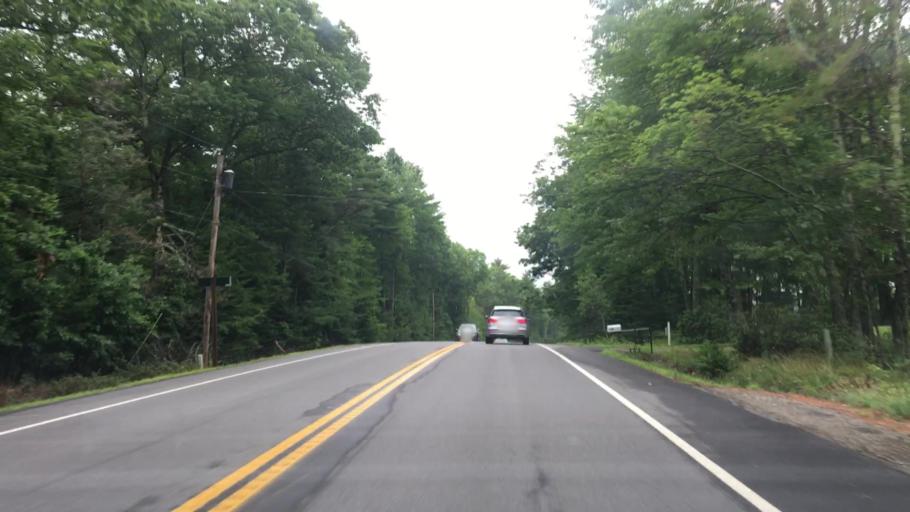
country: US
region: Maine
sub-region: Lincoln County
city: Jefferson
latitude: 44.2557
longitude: -69.4421
